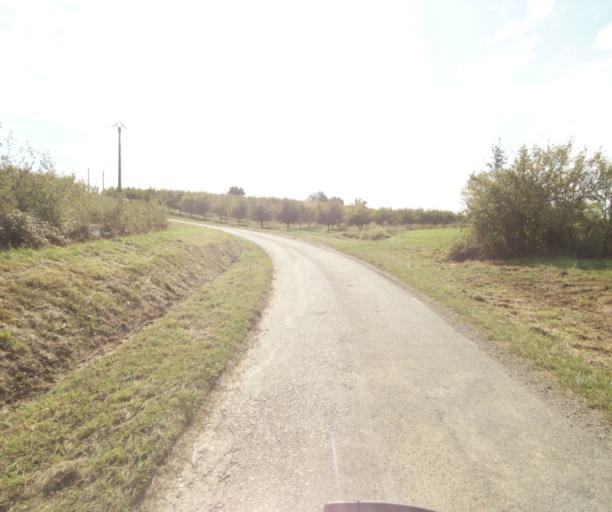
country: FR
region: Midi-Pyrenees
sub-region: Departement du Tarn-et-Garonne
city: Finhan
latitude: 43.8785
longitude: 1.1862
